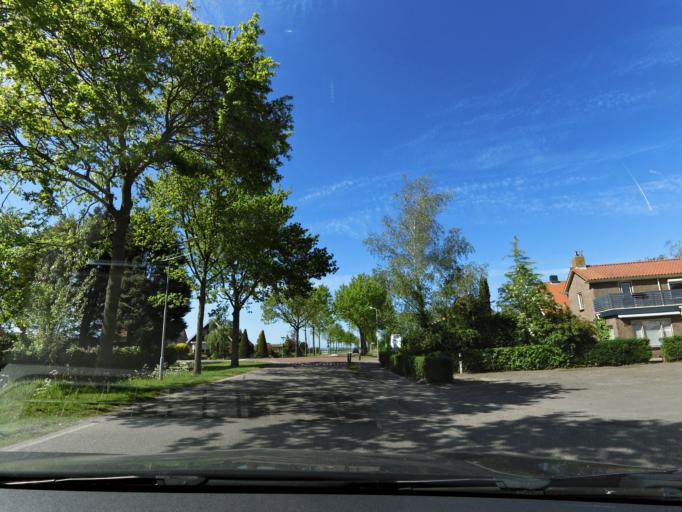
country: NL
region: Zeeland
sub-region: Schouwen-Duiveland
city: Bruinisse
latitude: 51.6490
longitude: 3.9960
